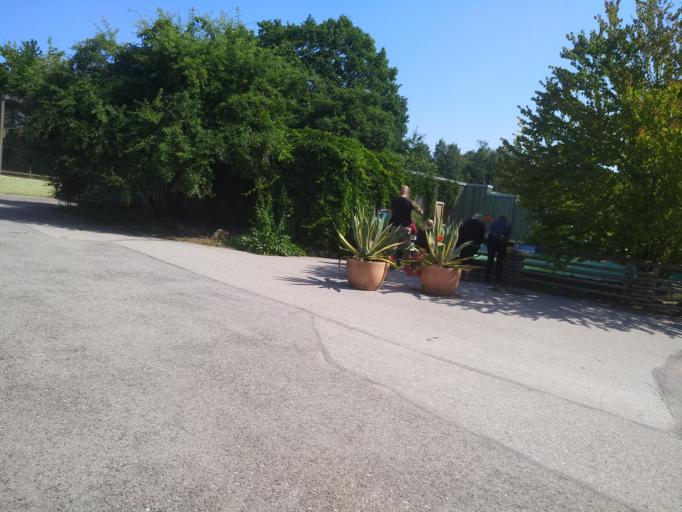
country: EE
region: Harju
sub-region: Saue vald
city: Laagri
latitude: 59.4220
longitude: 24.6602
